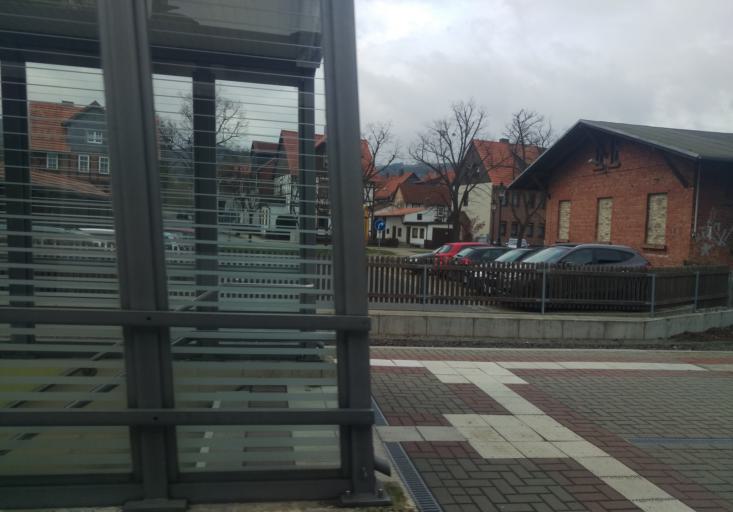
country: DE
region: Saxony-Anhalt
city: Ilsenburg
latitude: 51.8690
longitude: 10.6831
